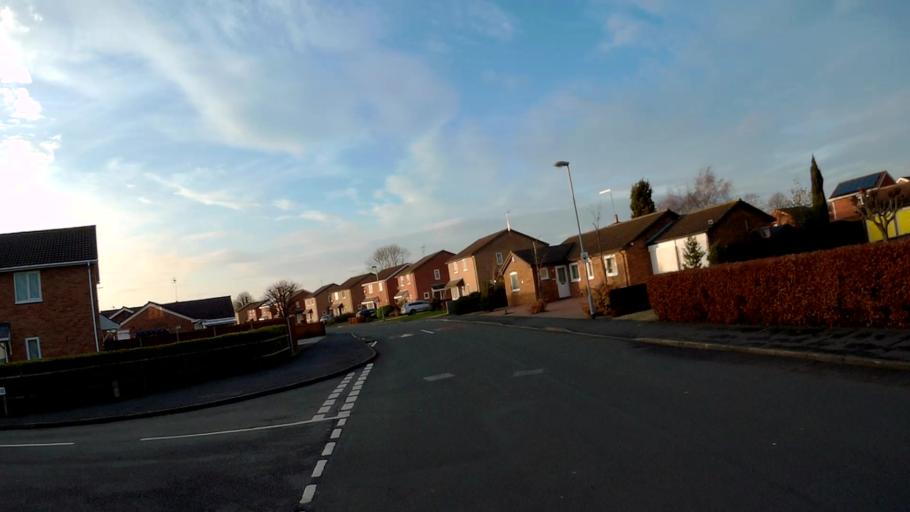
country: GB
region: England
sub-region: Lincolnshire
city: Bourne
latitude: 52.7740
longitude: -0.3830
